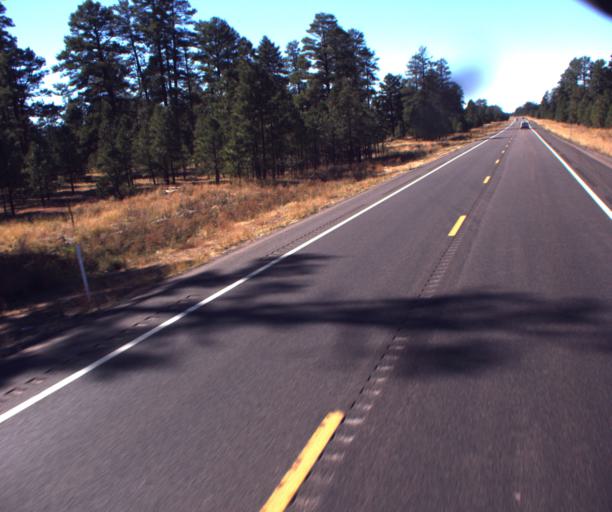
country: US
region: Arizona
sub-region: Apache County
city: Saint Michaels
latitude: 35.6949
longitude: -109.2705
